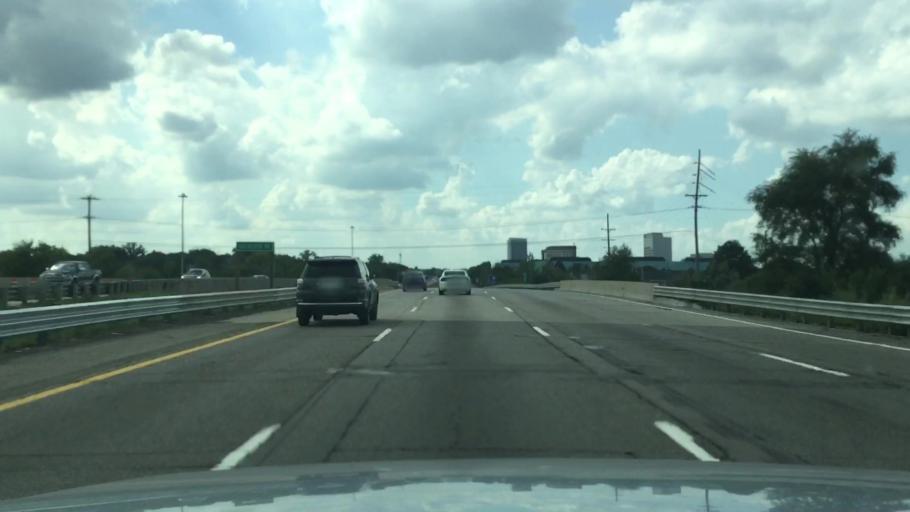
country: US
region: Michigan
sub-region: Oakland County
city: Clawson
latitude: 42.5585
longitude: -83.1279
